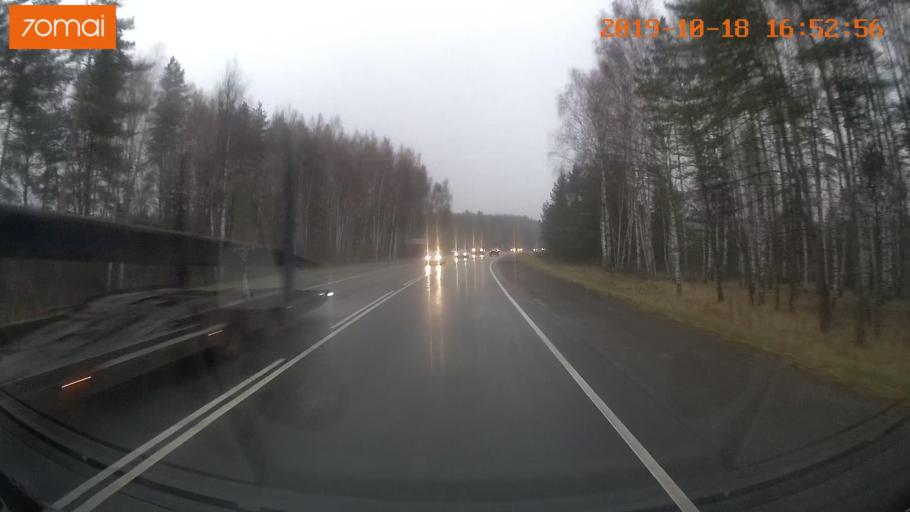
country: RU
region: Ivanovo
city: Nerl'
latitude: 56.6081
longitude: 40.5560
